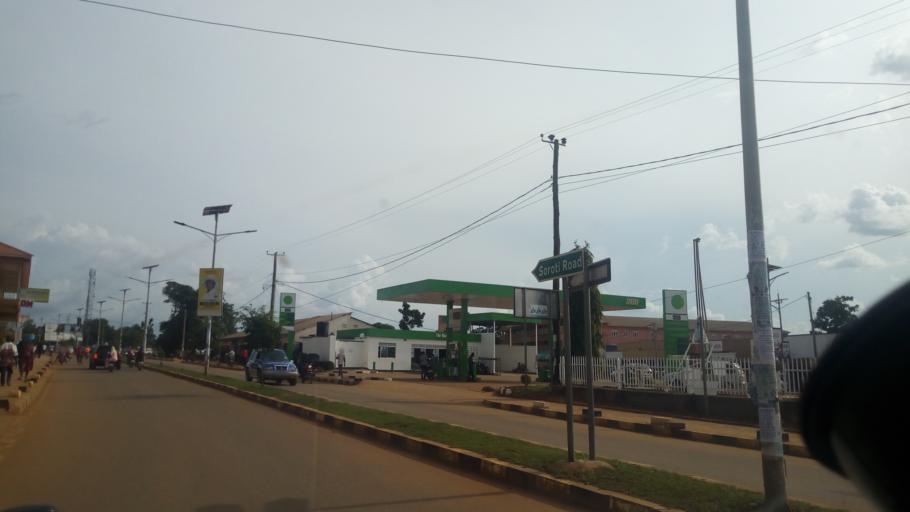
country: UG
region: Northern Region
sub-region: Lira District
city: Lira
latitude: 2.2378
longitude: 32.8938
